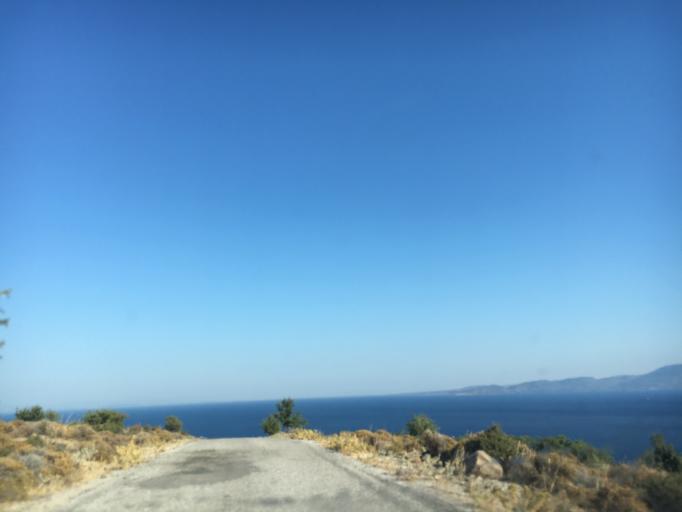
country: TR
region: Canakkale
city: Behram
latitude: 39.4885
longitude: 26.2616
